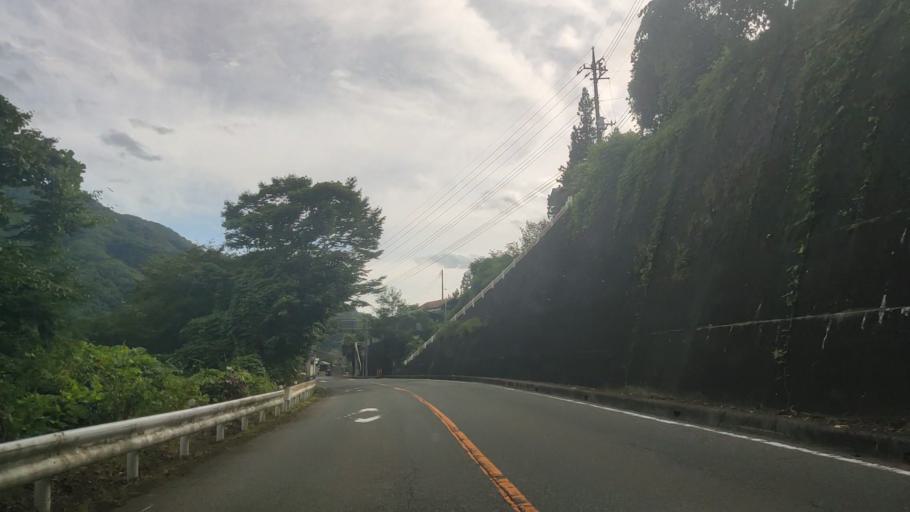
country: JP
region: Gunma
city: Kiryu
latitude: 36.5826
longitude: 139.3958
